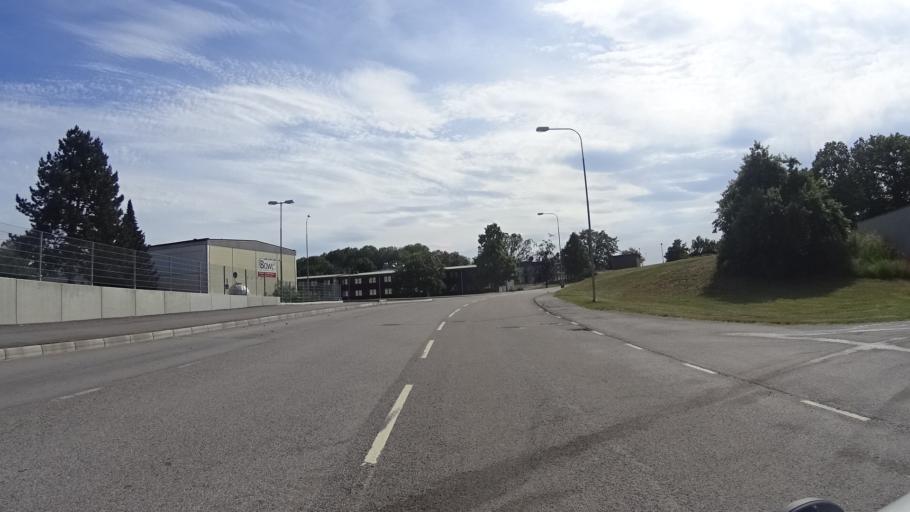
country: SE
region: Kalmar
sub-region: Vasterviks Kommun
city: Gamleby
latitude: 57.8911
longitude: 16.4160
